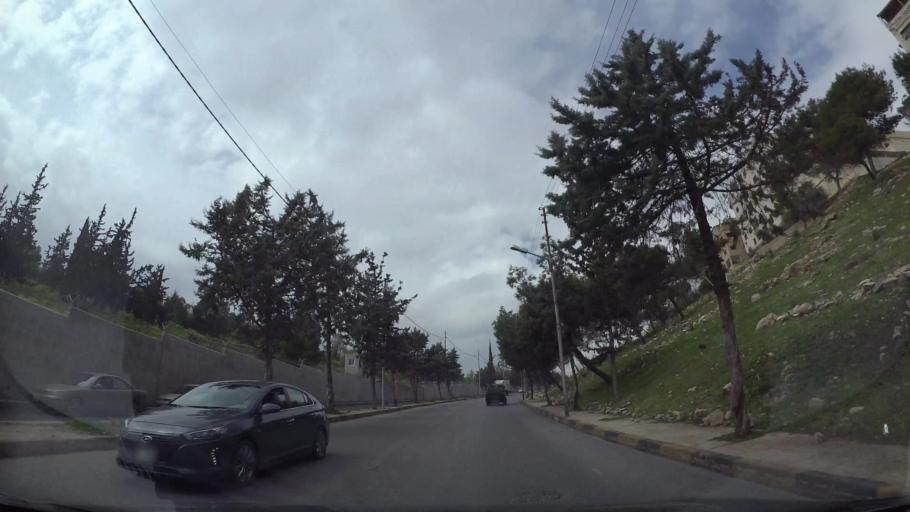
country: JO
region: Amman
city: Amman
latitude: 31.9603
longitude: 35.9519
